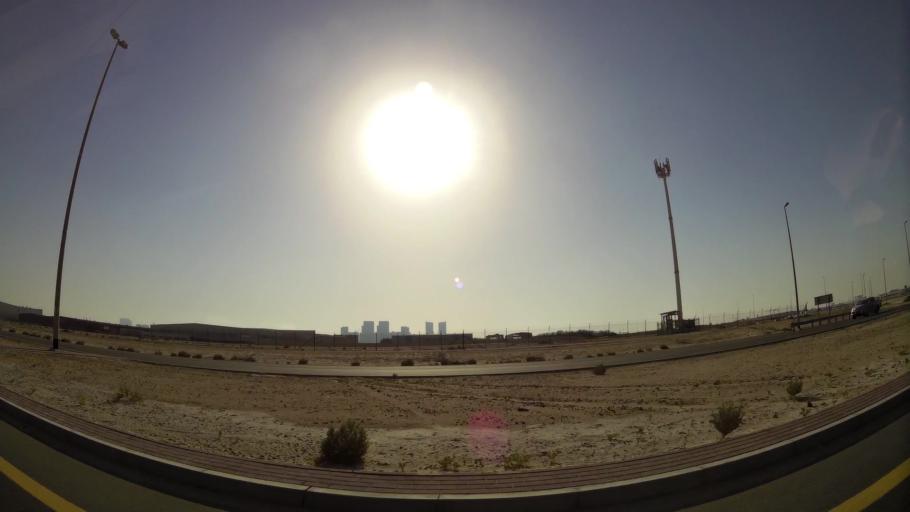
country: AE
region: Dubai
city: Dubai
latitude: 24.9789
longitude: 55.1140
